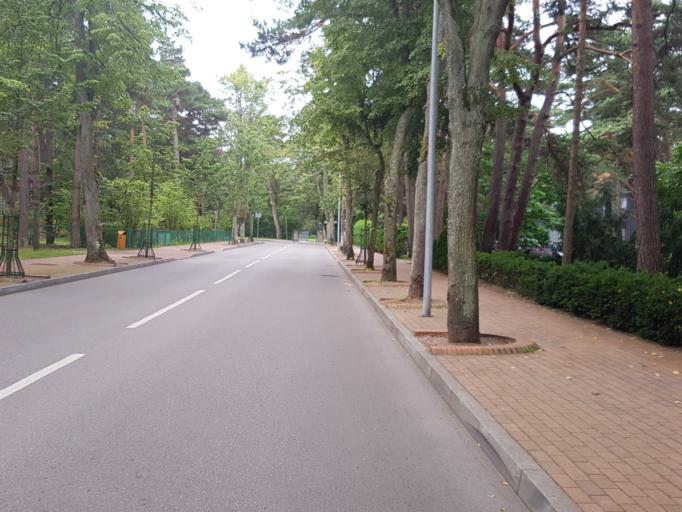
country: LT
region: Klaipedos apskritis
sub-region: Klaipeda
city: Palanga
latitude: 55.9133
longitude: 21.0557
